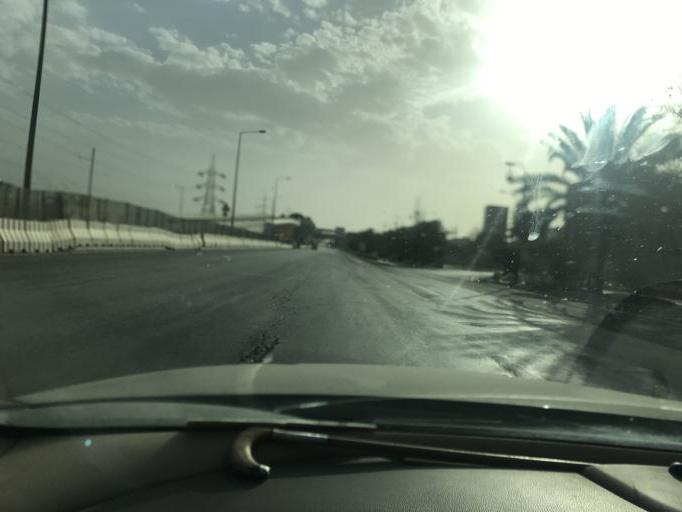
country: SA
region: Ar Riyad
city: Riyadh
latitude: 24.8036
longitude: 46.7009
